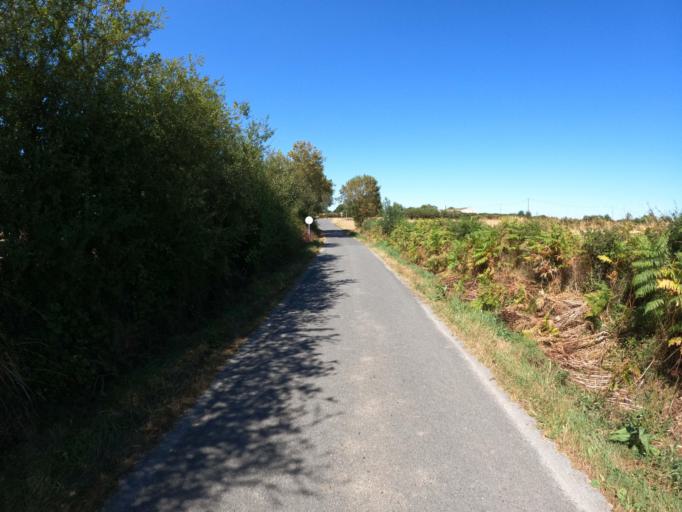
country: FR
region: Pays de la Loire
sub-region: Departement de Maine-et-Loire
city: La Seguiniere
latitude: 47.0561
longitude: -0.9700
